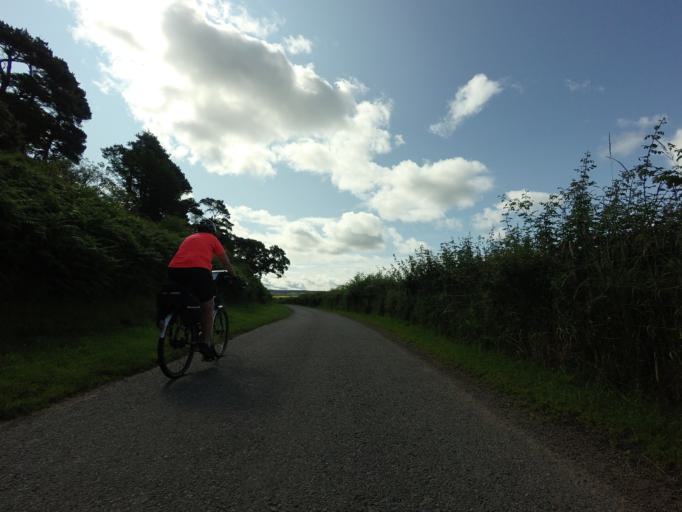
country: GB
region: Scotland
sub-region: Moray
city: Kinloss
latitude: 57.6391
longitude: -3.5212
